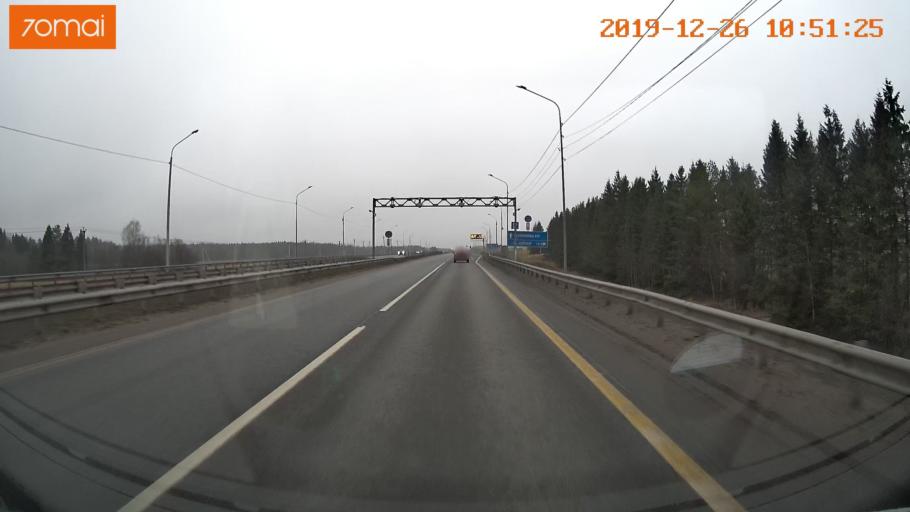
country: RU
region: Vologda
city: Molochnoye
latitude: 59.2037
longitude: 39.6629
